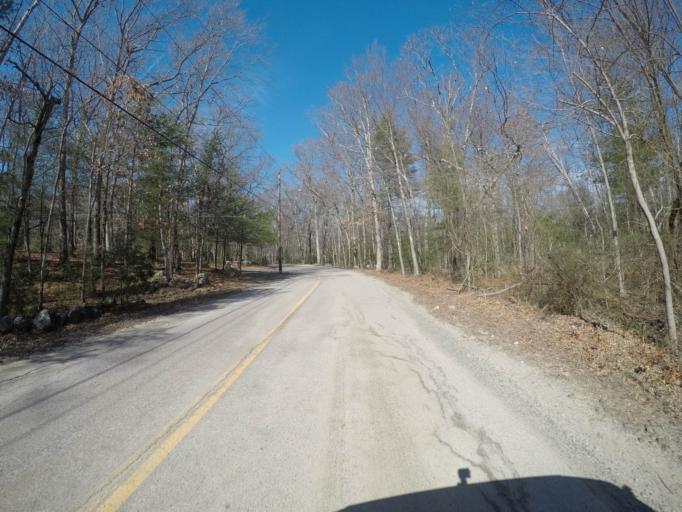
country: US
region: Massachusetts
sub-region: Norfolk County
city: Sharon
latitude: 42.0906
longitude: -71.1527
